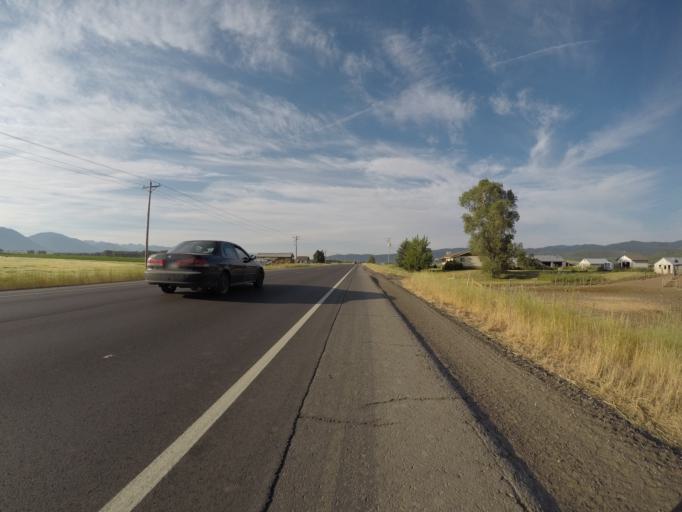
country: US
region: Wyoming
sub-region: Lincoln County
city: Afton
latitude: 42.9617
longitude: -111.0124
